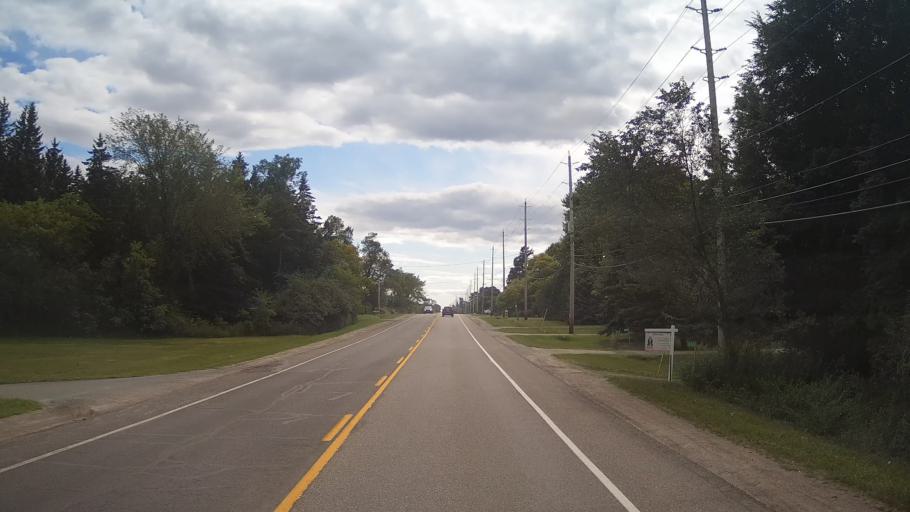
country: CA
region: Ontario
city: Kingston
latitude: 44.2825
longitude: -76.4362
